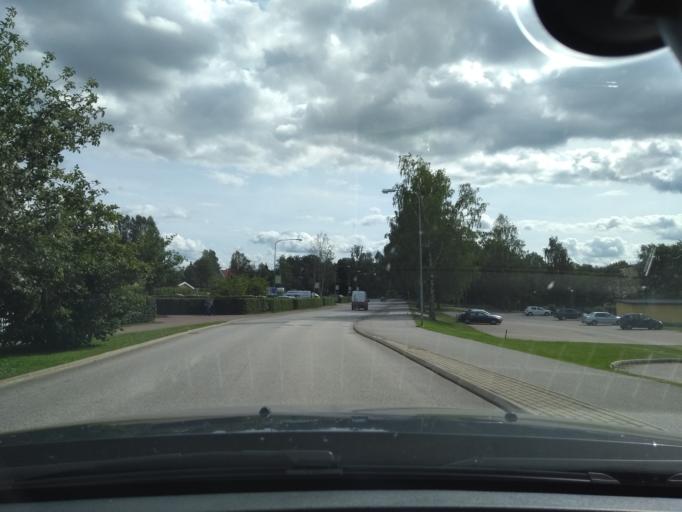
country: SE
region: Kalmar
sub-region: Vimmerby Kommun
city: Vimmerby
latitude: 57.6745
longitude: 15.8557
